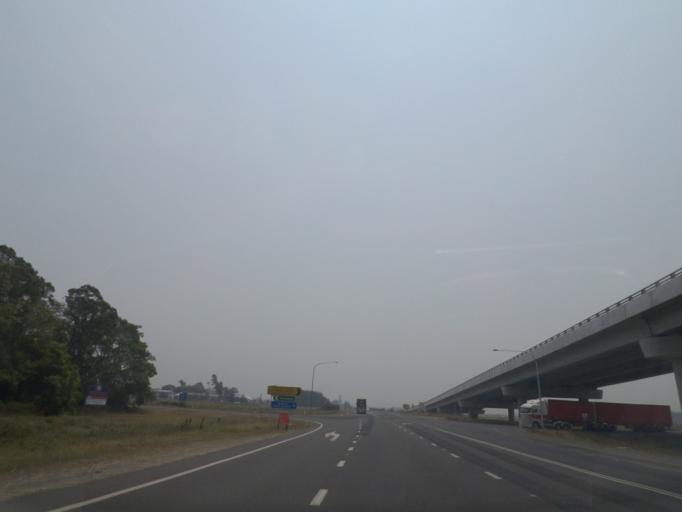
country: AU
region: New South Wales
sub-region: Clarence Valley
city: Maclean
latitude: -29.4255
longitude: 153.2411
